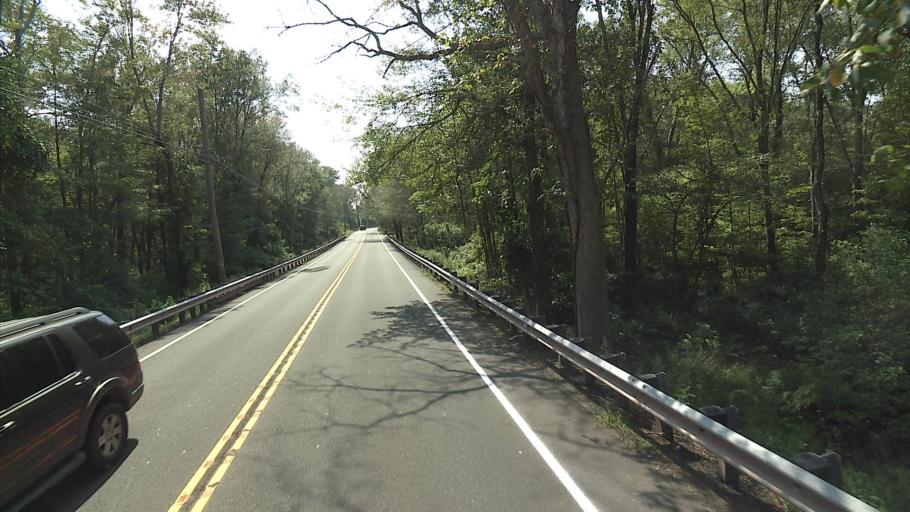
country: US
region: Connecticut
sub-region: Middlesex County
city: Durham
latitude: 41.4315
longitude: -72.6501
